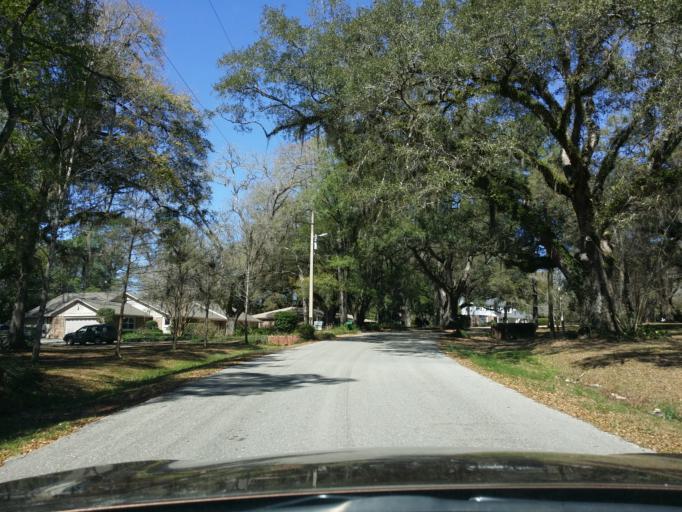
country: US
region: Florida
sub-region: Leon County
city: Tallahassee
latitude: 30.4840
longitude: -84.1844
